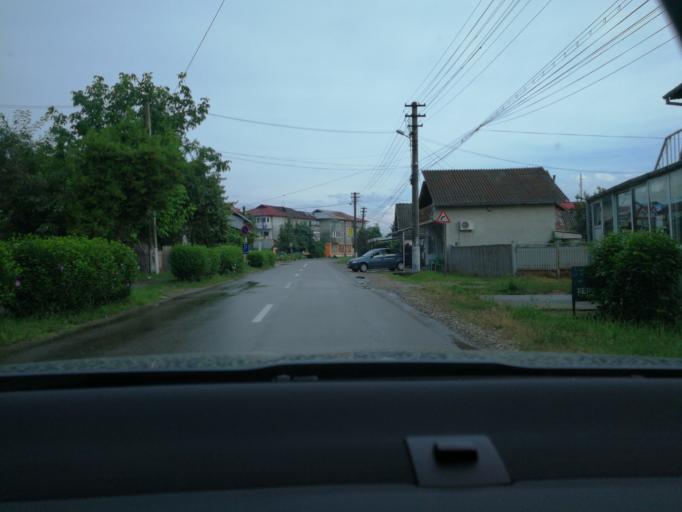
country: RO
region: Prahova
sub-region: Comuna Ceptura
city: Ceptura de Jos
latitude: 45.0187
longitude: 26.3272
